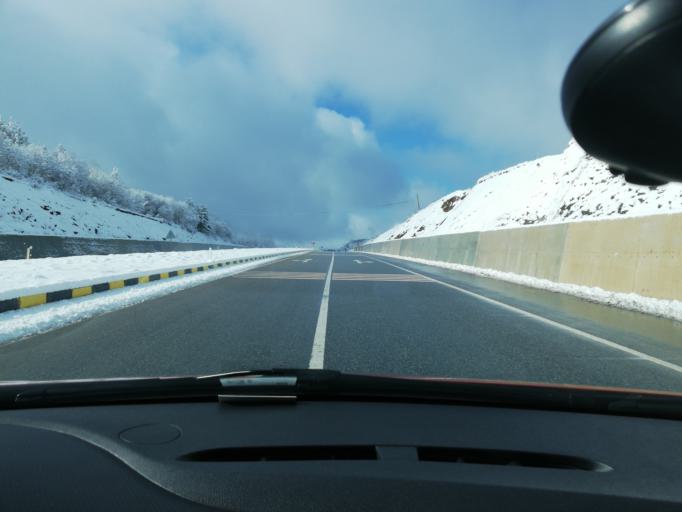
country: TR
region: Kastamonu
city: Kuzyaka
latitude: 41.3334
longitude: 33.6230
